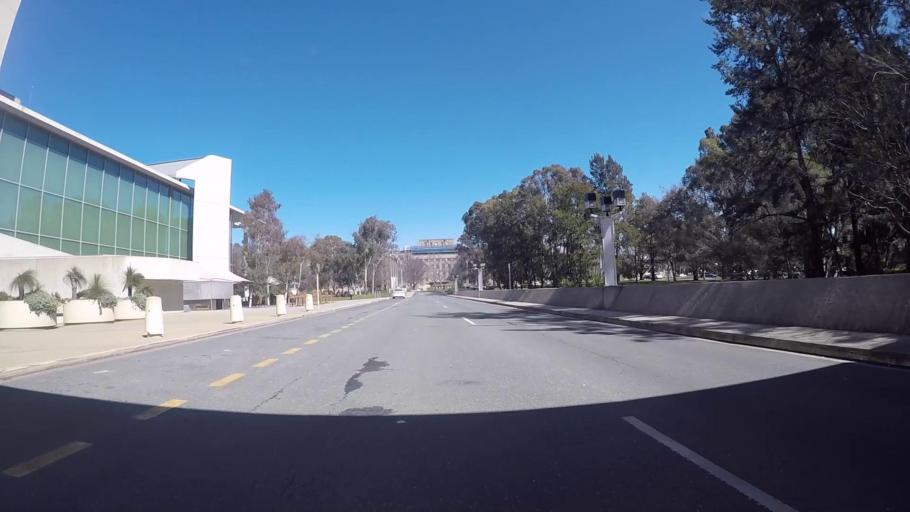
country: AU
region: Australian Capital Territory
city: Forrest
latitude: -35.3002
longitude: 149.1361
